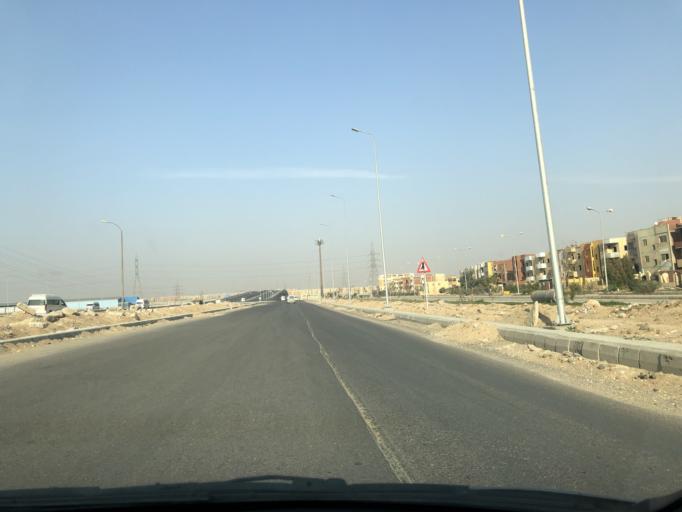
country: EG
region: Al Jizah
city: Madinat Sittah Uktubar
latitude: 29.9074
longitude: 30.9237
